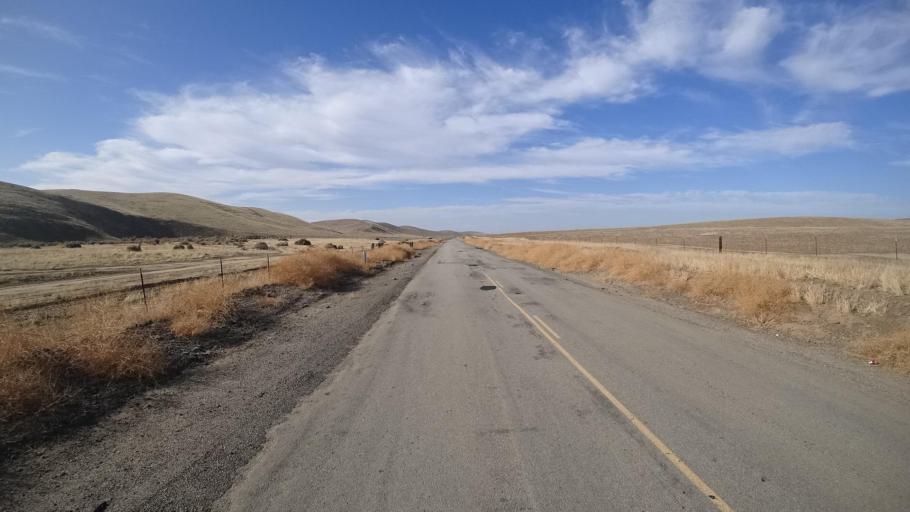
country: US
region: California
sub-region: Tulare County
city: Richgrove
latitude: 35.6258
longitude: -118.9973
